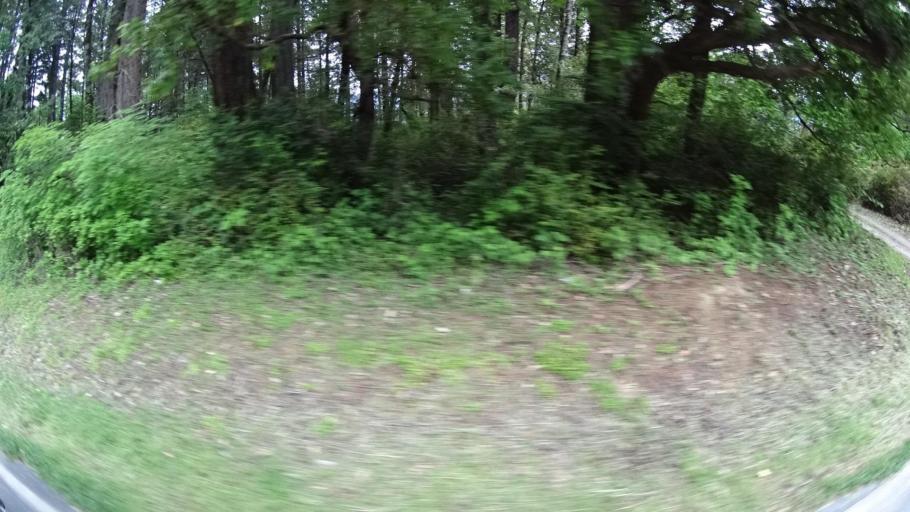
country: US
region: California
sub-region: Humboldt County
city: Willow Creek
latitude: 41.0825
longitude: -123.7031
